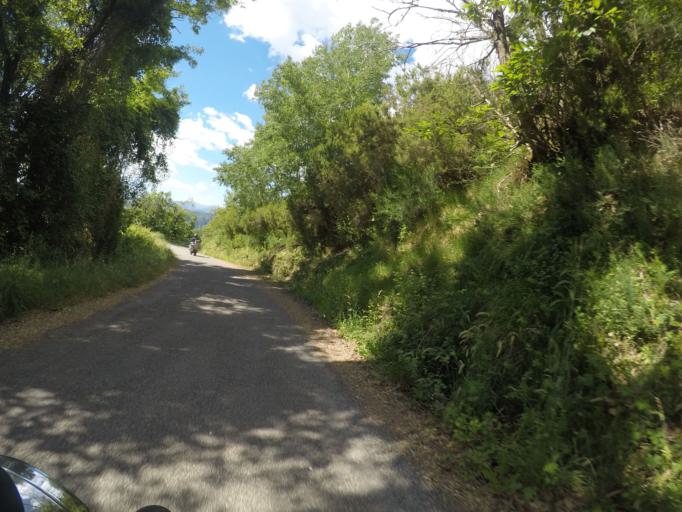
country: IT
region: Tuscany
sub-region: Provincia di Massa-Carrara
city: Casola in Lunigiana
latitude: 44.1773
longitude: 10.1556
